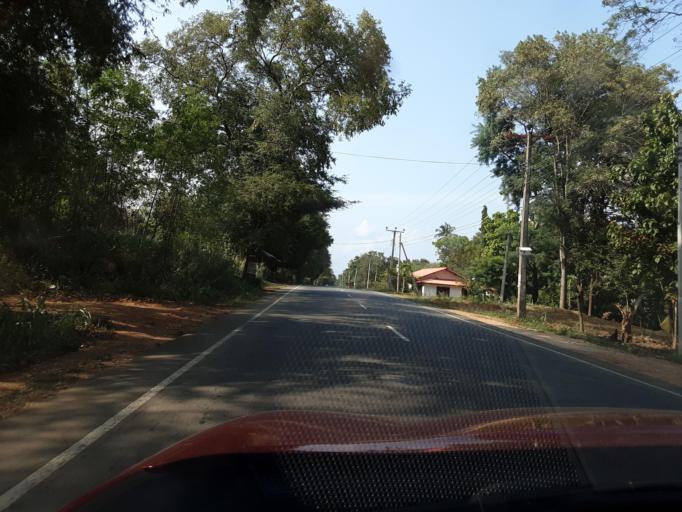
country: LK
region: Uva
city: Haputale
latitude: 6.5796
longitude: 81.1403
